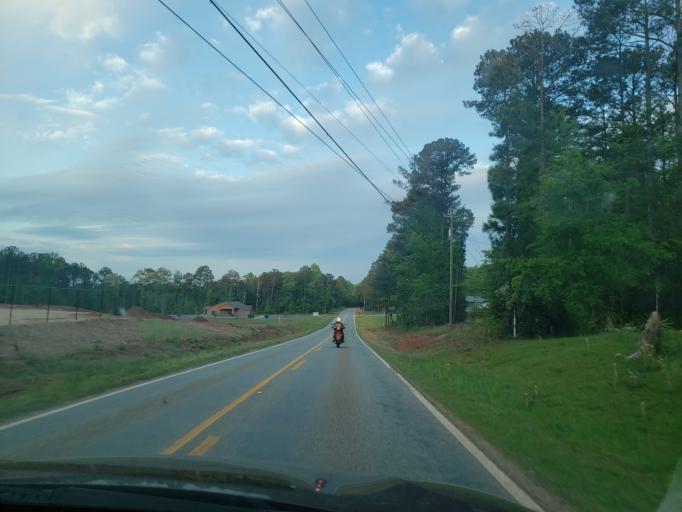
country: US
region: Alabama
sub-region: Tallapoosa County
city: Dadeville
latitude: 32.7083
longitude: -85.7974
